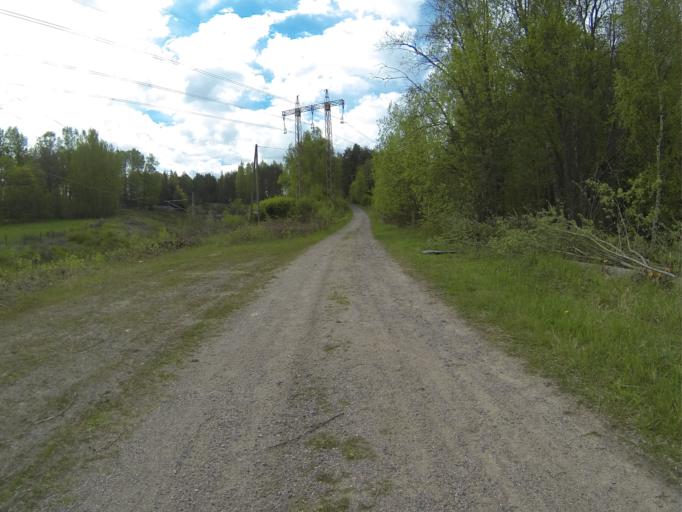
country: FI
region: Varsinais-Suomi
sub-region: Salo
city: Salo
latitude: 60.3568
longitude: 23.1172
